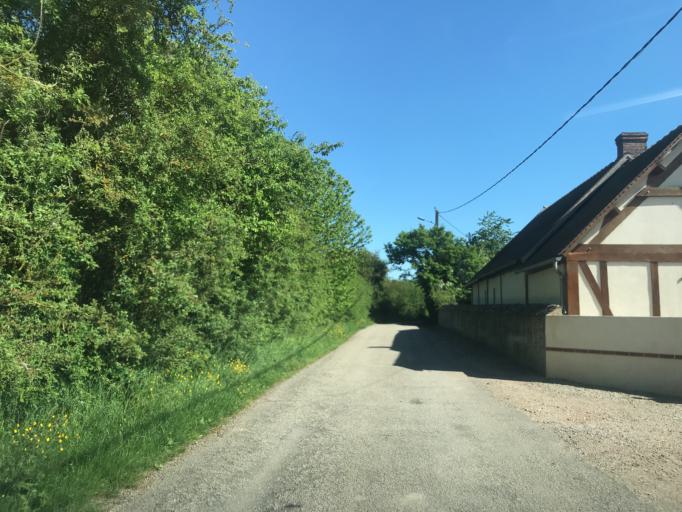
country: FR
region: Haute-Normandie
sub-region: Departement de l'Eure
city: Verneuil-sur-Avre
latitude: 48.7480
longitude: 0.9853
